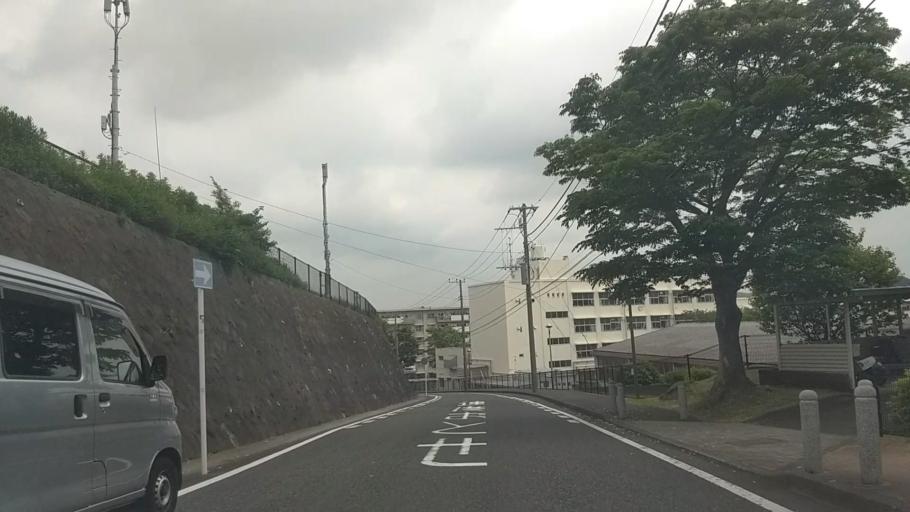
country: JP
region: Kanagawa
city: Kamakura
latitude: 35.3722
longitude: 139.5341
